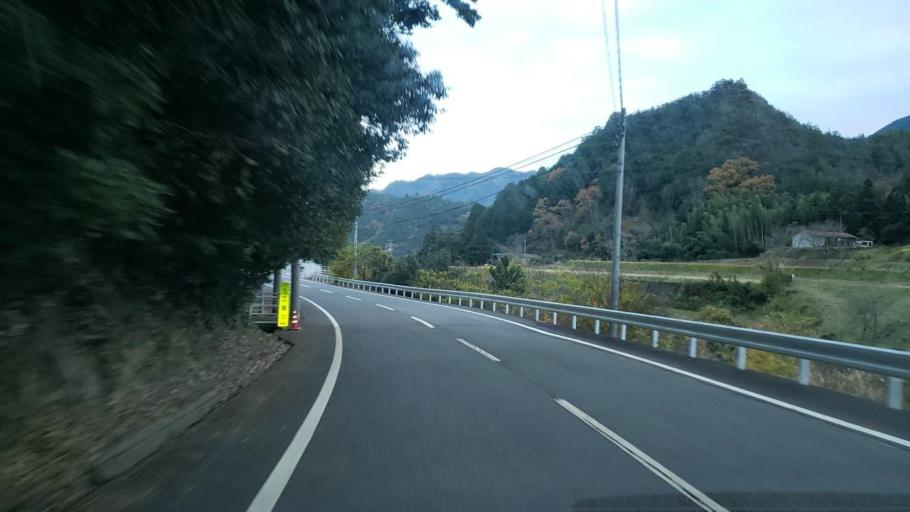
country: JP
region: Tokushima
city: Kamojimacho-jogejima
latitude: 34.1984
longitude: 134.2777
